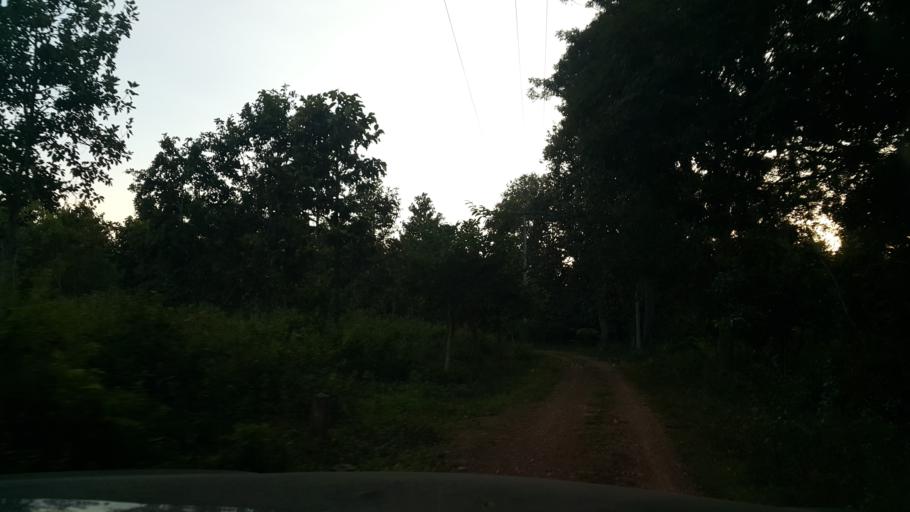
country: TH
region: Chiang Mai
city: Mae On
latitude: 18.6953
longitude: 99.2033
